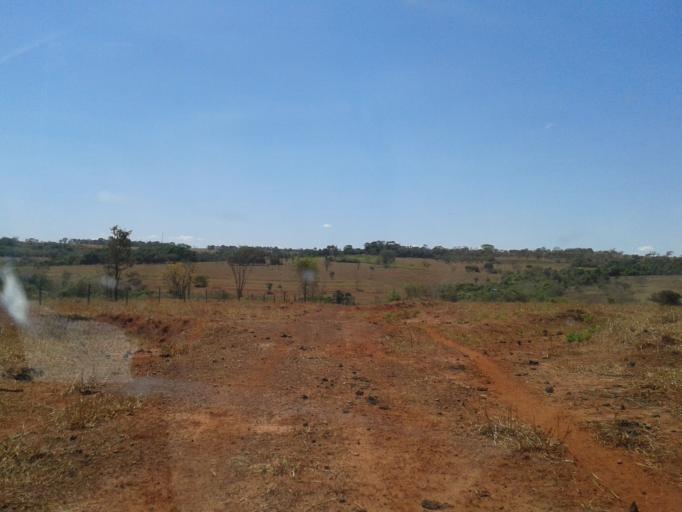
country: BR
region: Minas Gerais
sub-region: Monte Alegre De Minas
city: Monte Alegre de Minas
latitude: -18.7986
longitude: -49.0773
